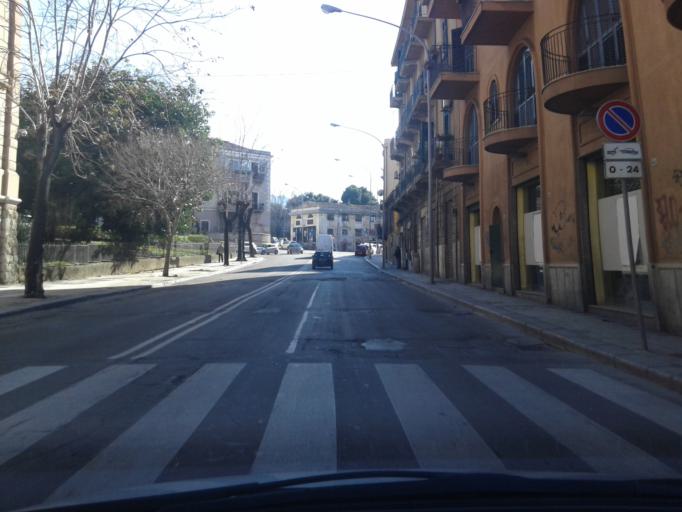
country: IT
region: Sicily
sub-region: Palermo
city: Palermo
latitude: 38.1131
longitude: 13.3523
